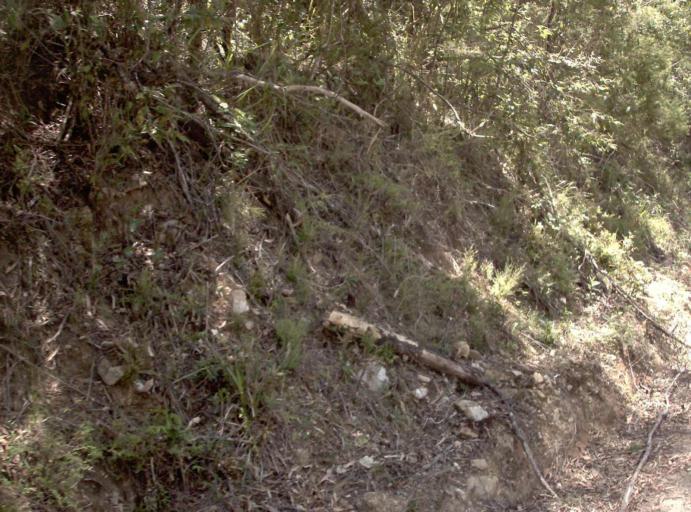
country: AU
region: New South Wales
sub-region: Bombala
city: Bombala
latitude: -37.4598
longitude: 148.9372
